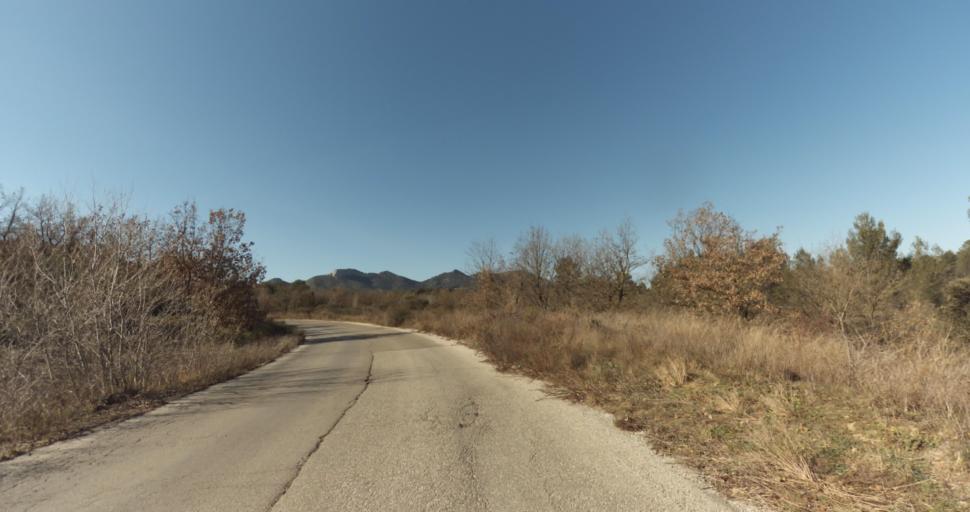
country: FR
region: Provence-Alpes-Cote d'Azur
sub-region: Departement des Bouches-du-Rhone
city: Peypin
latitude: 43.3951
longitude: 5.5781
